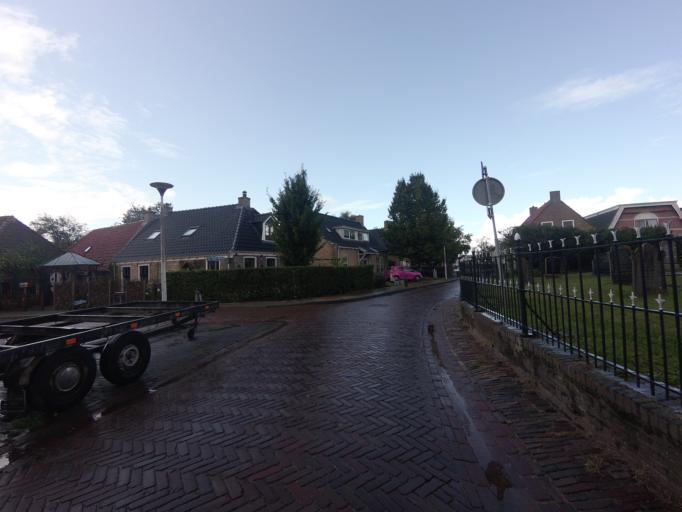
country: NL
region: Friesland
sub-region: Gemeente Boarnsterhim
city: Warten
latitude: 53.1494
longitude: 5.8973
